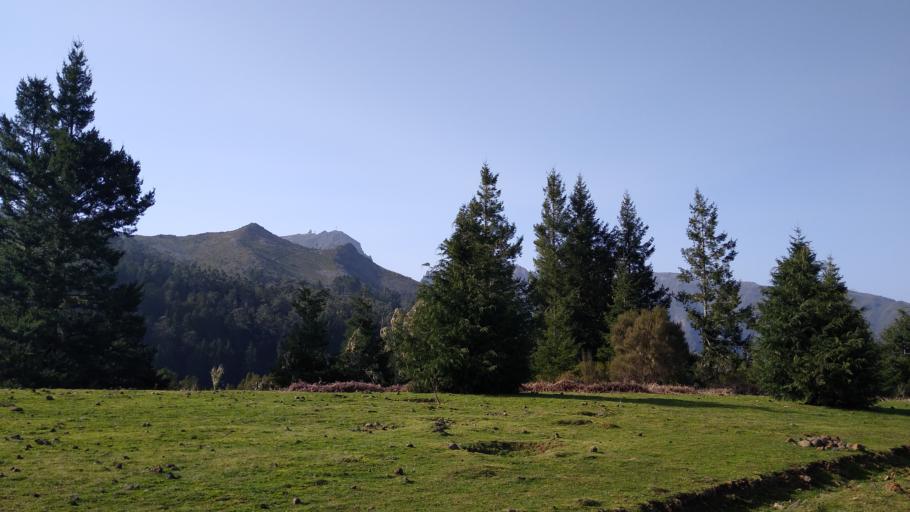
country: PT
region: Madeira
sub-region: Funchal
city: Nossa Senhora do Monte
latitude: 32.7260
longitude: -16.8869
